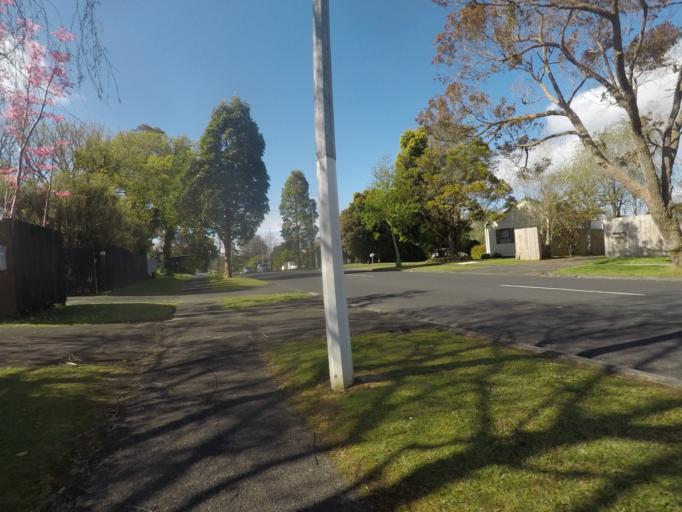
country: NZ
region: Auckland
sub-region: Auckland
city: Rosebank
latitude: -36.8625
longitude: 174.5982
